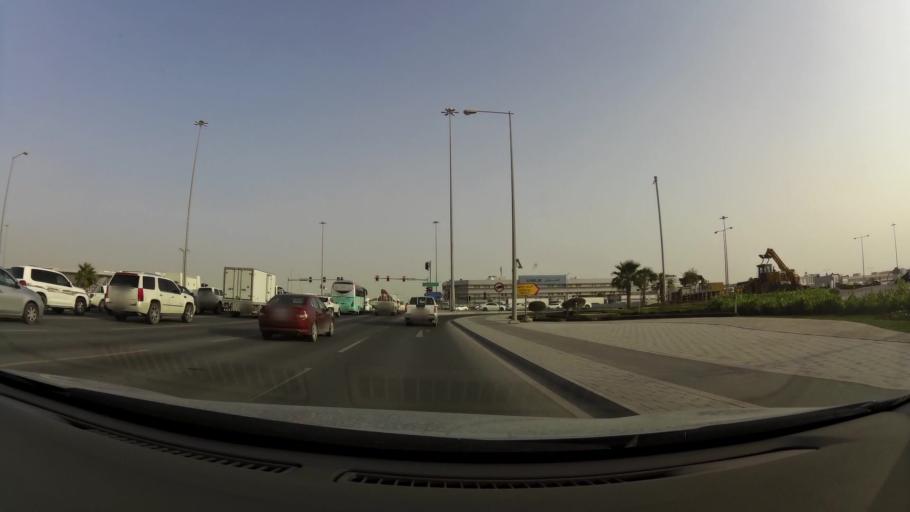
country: QA
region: Baladiyat ar Rayyan
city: Ar Rayyan
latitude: 25.2449
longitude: 51.4629
